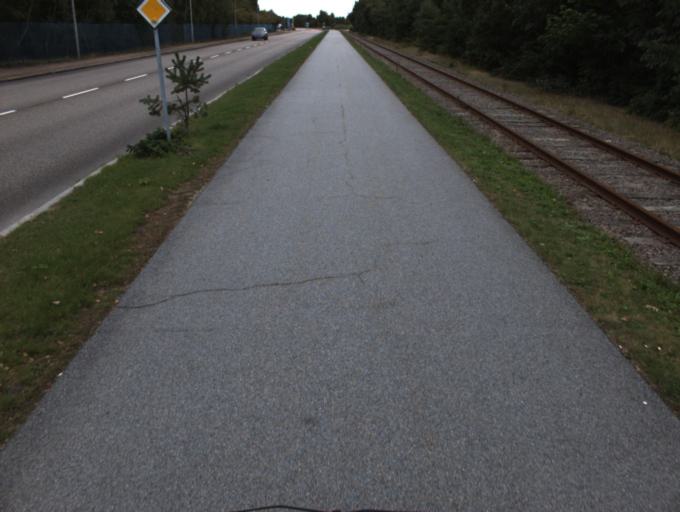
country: SE
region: Skane
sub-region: Helsingborg
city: Helsingborg
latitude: 56.0160
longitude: 12.7158
